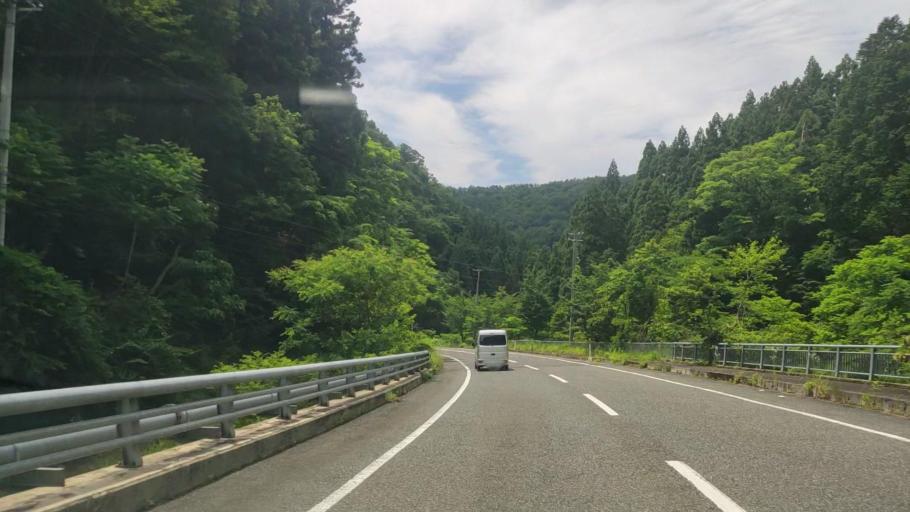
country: JP
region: Hyogo
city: Toyooka
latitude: 35.4845
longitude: 134.6145
